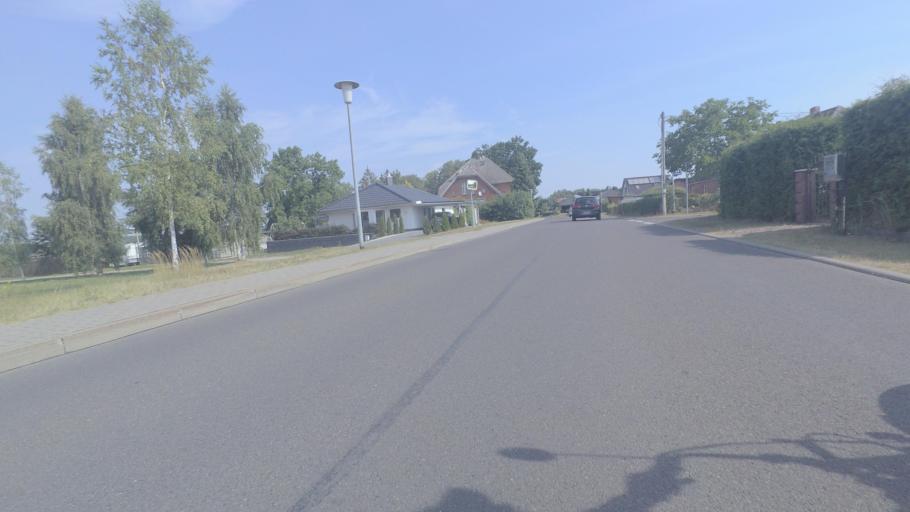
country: DE
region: Mecklenburg-Vorpommern
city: Wendorf
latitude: 54.2379
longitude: 13.0724
